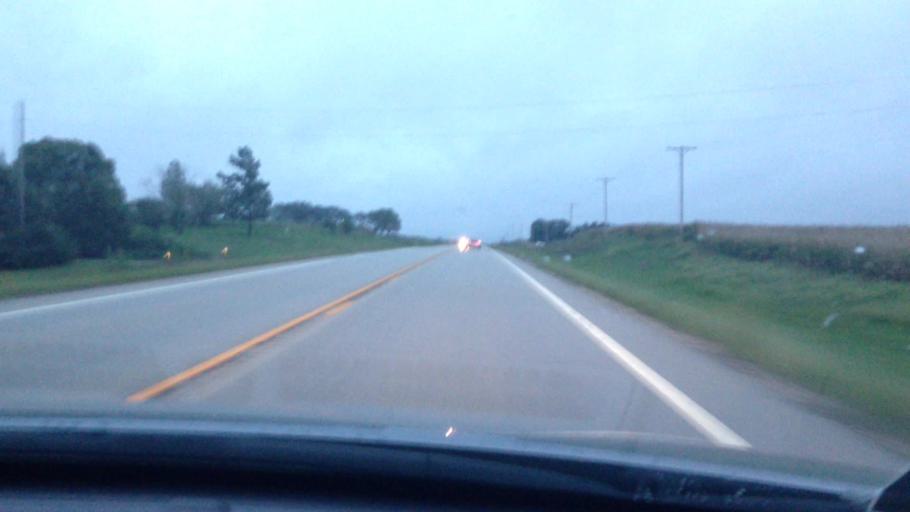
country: US
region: Kansas
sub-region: Brown County
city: Horton
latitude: 39.6665
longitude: -95.4637
